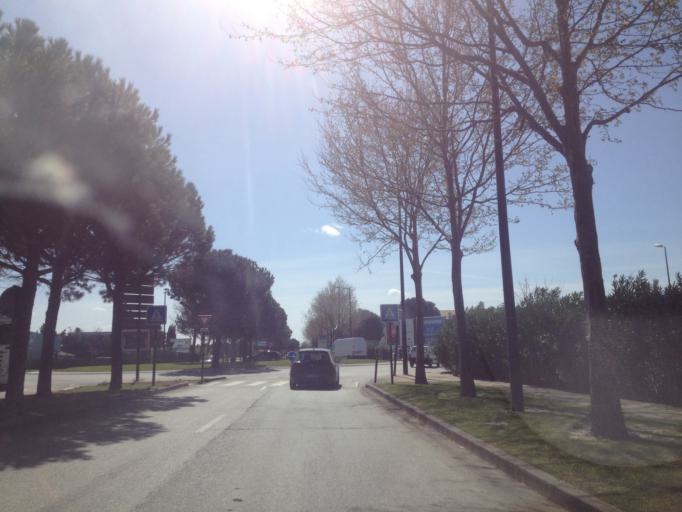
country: FR
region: Provence-Alpes-Cote d'Azur
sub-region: Departement du Vaucluse
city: Avignon
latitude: 43.9309
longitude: 4.7838
